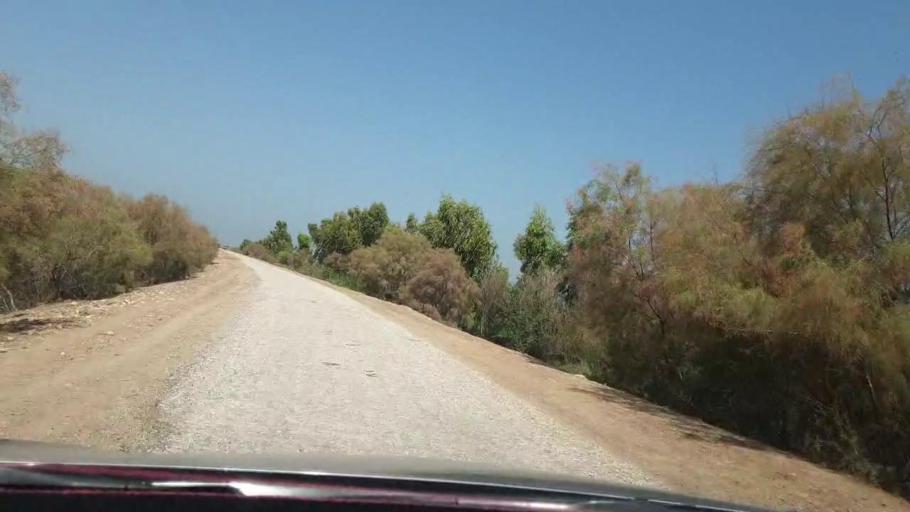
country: PK
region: Sindh
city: Warah
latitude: 27.5372
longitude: 67.7399
